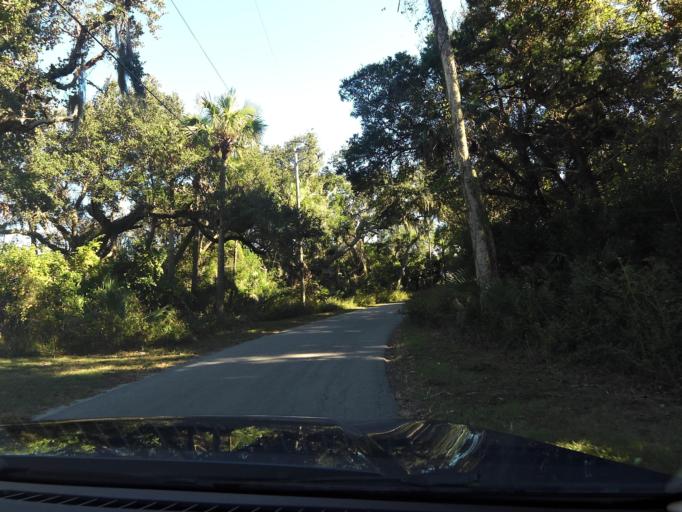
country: US
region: Florida
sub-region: Duval County
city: Atlantic Beach
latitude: 30.4220
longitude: -81.4268
